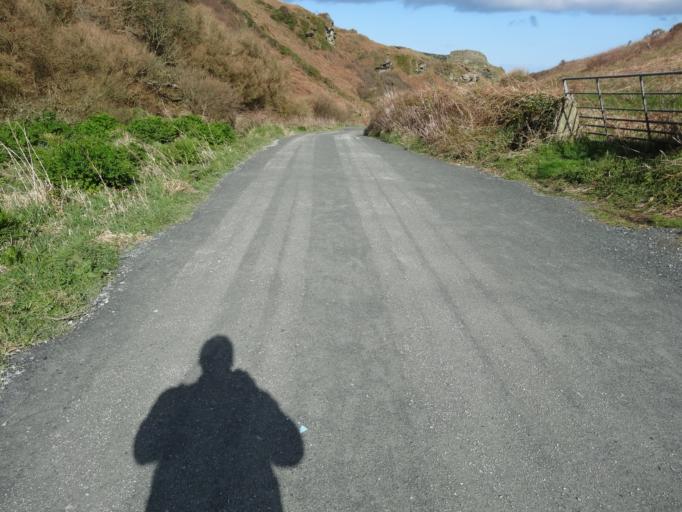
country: GB
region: England
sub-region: Cornwall
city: Tintagel
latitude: 50.6649
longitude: -4.7560
